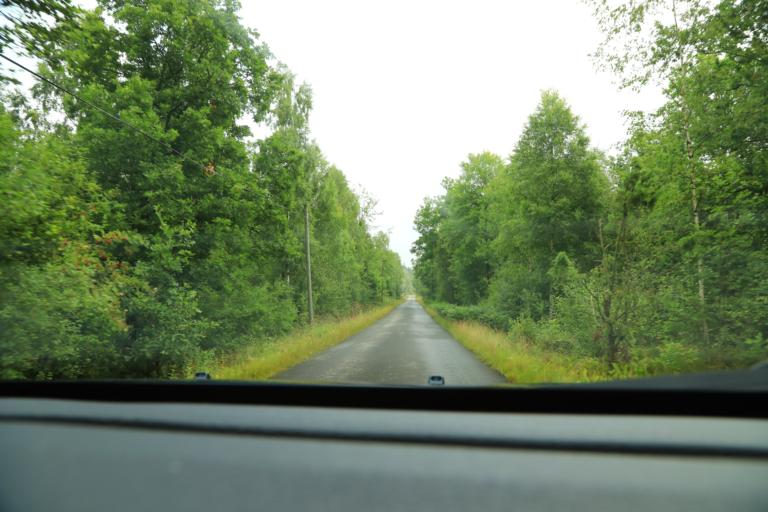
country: SE
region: Halland
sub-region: Falkenbergs Kommun
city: Falkenberg
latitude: 57.1183
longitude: 12.6929
